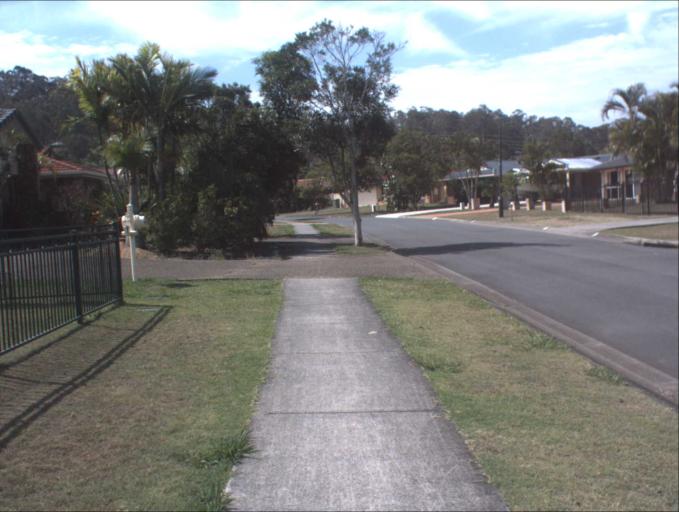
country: AU
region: Queensland
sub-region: Logan
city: Slacks Creek
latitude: -27.6801
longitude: 153.1741
